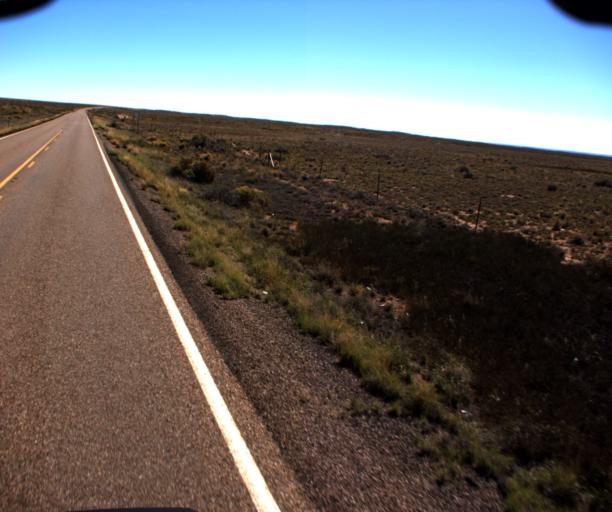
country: US
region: Arizona
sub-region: Navajo County
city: Holbrook
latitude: 35.0446
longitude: -110.0933
